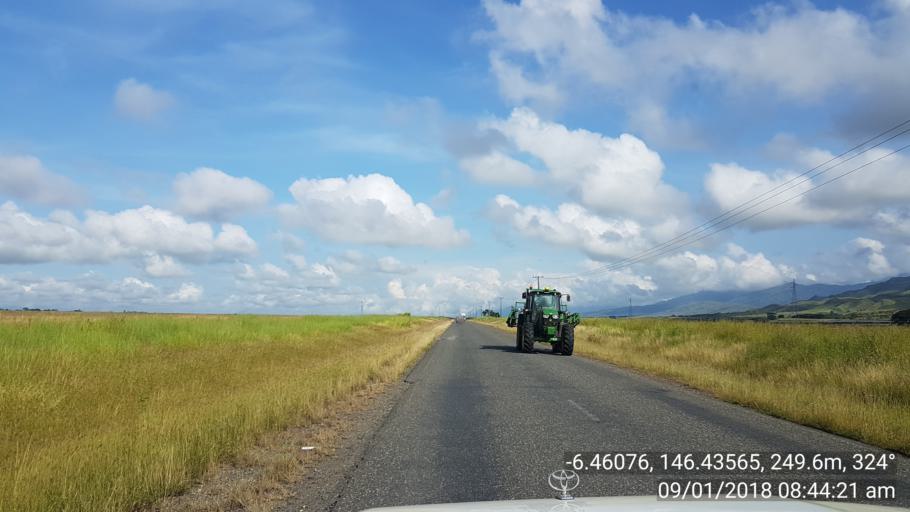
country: PG
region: Eastern Highlands
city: Kainantu
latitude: -6.4608
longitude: 146.4356
